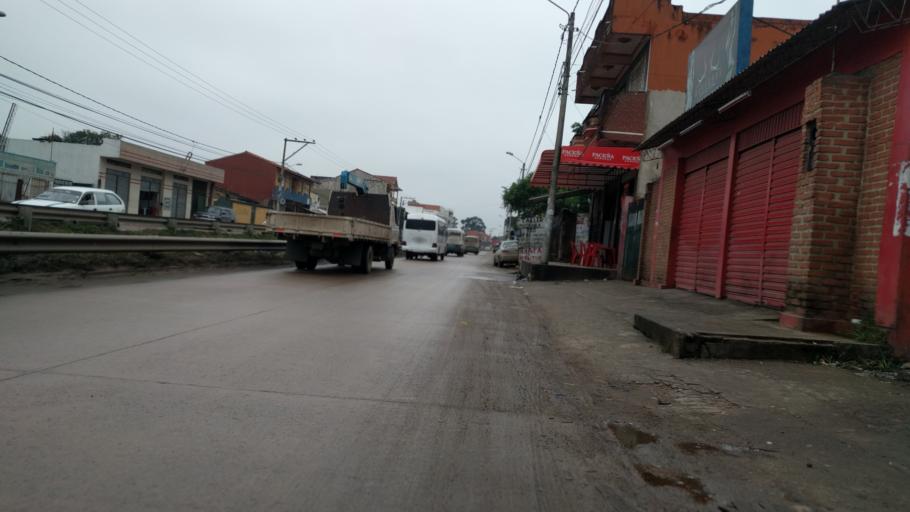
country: BO
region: Santa Cruz
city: Santa Cruz de la Sierra
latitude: -17.8281
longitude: -63.1710
